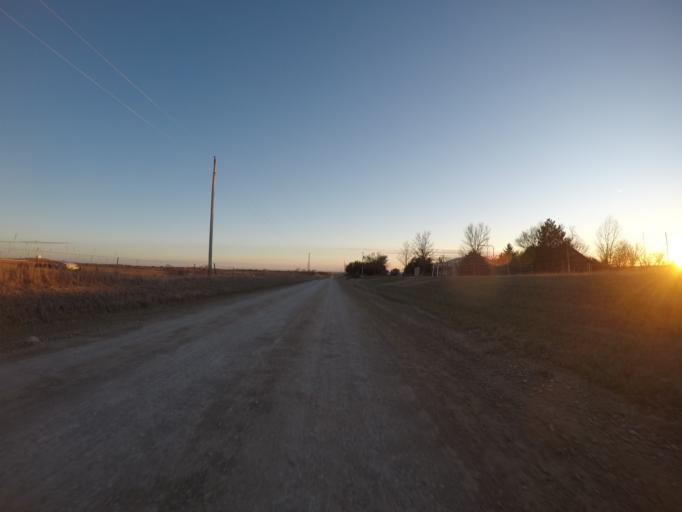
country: US
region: Kansas
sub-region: Riley County
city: Manhattan
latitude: 39.2681
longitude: -96.4827
